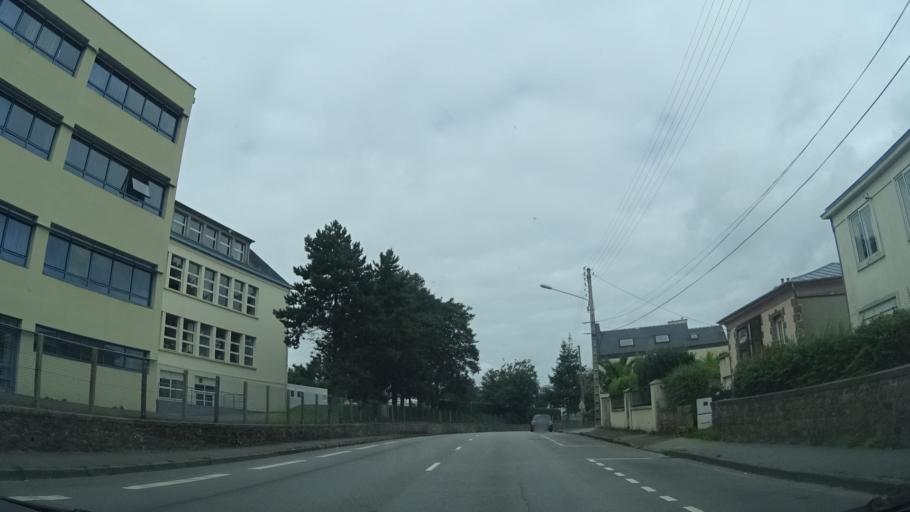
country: FR
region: Brittany
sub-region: Departement du Finistere
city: Brest
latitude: 48.4033
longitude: -4.4575
